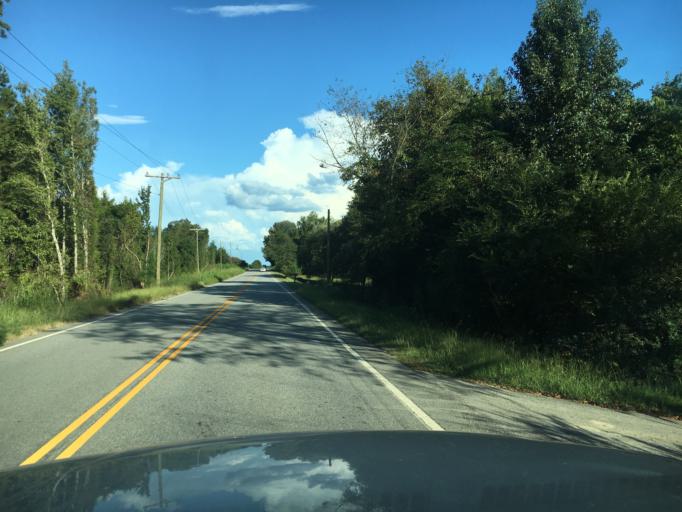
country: US
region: South Carolina
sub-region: Greenville County
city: Five Forks
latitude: 34.7976
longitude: -82.1478
